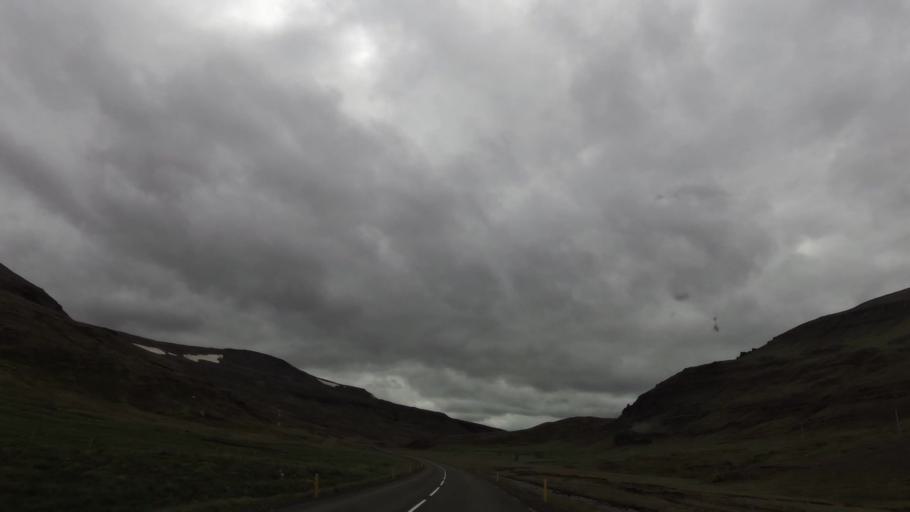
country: IS
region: West
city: Borgarnes
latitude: 65.3490
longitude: -21.7647
